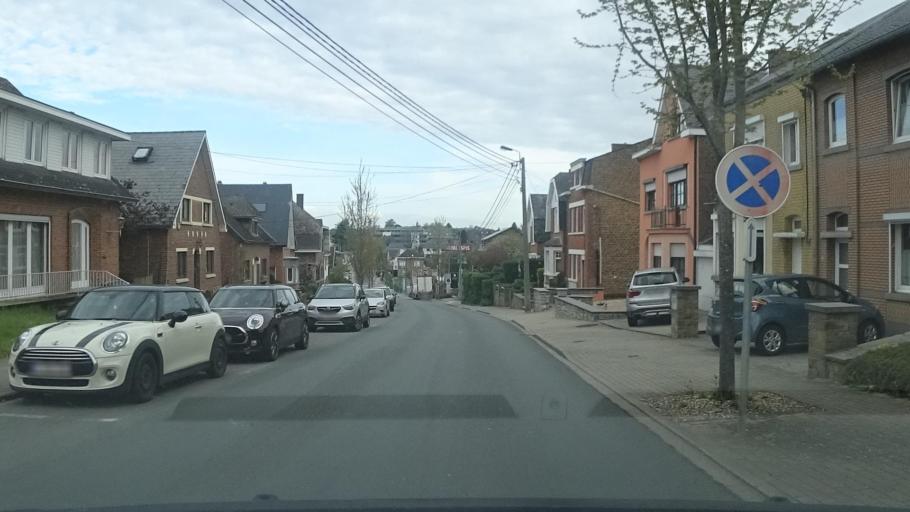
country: BE
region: Wallonia
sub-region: Province de Namur
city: Namur
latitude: 50.4761
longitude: 4.8843
